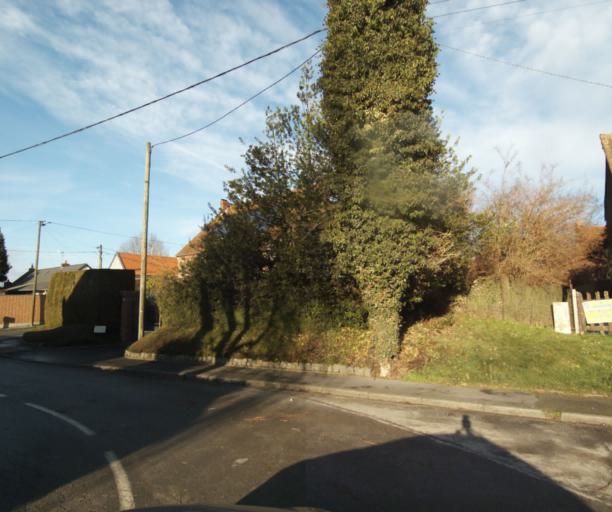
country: FR
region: Nord-Pas-de-Calais
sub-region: Departement du Nord
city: Curgies
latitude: 50.3519
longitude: 3.5980
